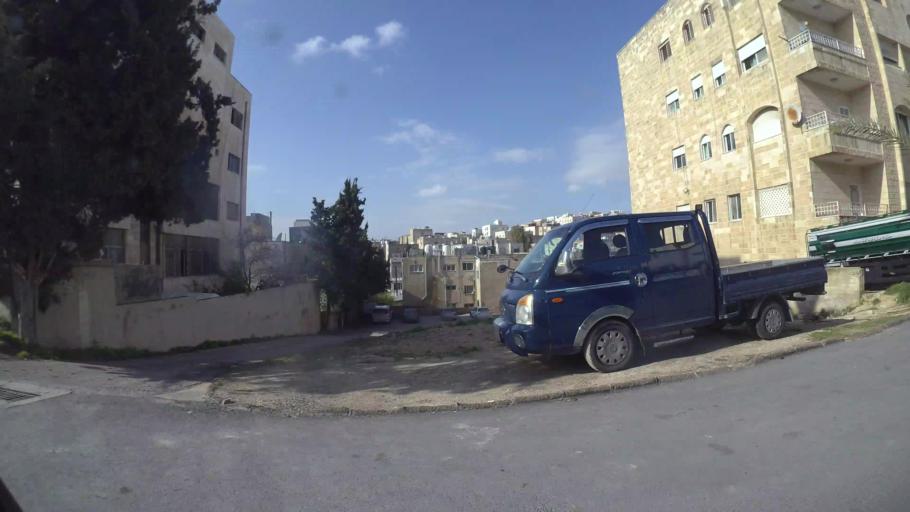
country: JO
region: Amman
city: Al Jubayhah
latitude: 32.0222
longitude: 35.8488
